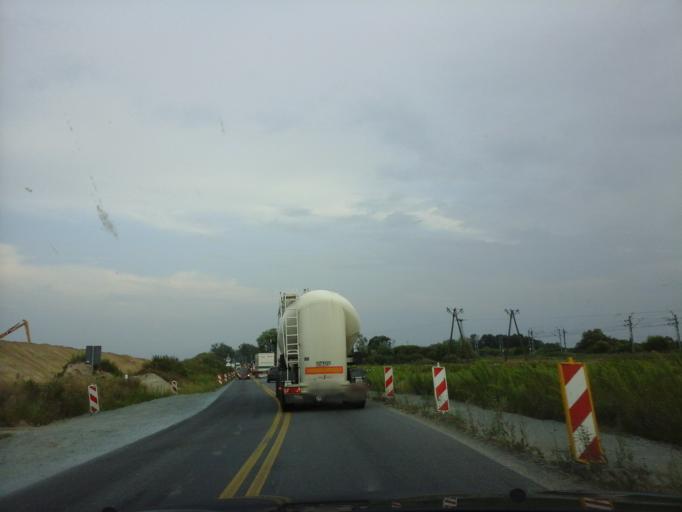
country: PL
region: Lower Silesian Voivodeship
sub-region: Powiat trzebnicki
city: Zmigrod
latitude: 51.5107
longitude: 16.8925
